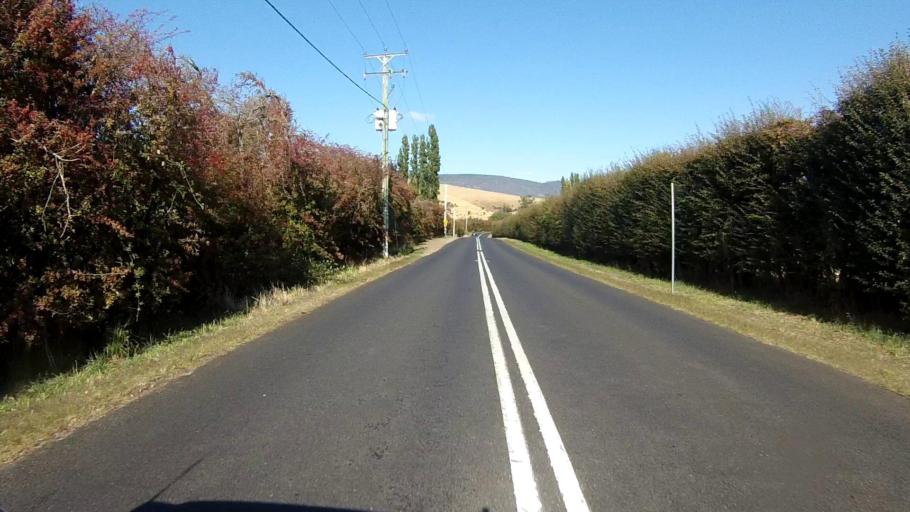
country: AU
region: Tasmania
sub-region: Derwent Valley
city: New Norfolk
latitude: -42.7387
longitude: 146.9567
